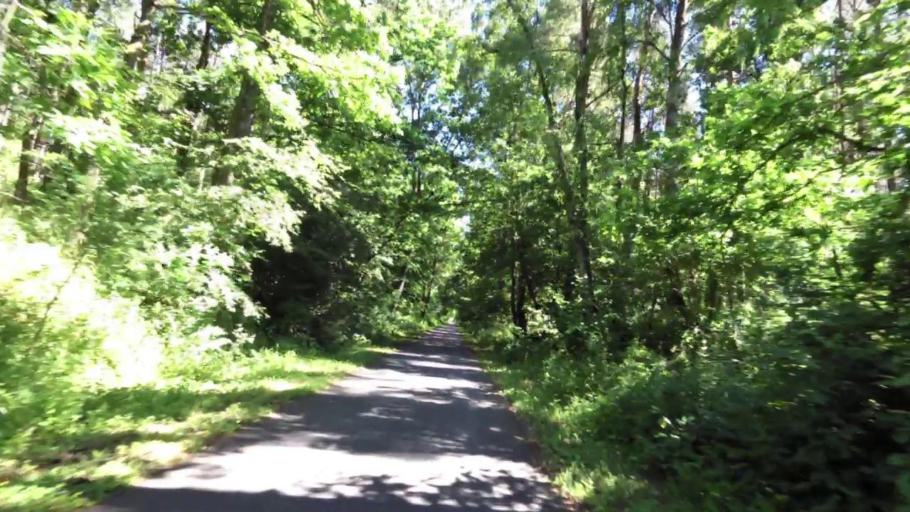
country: PL
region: West Pomeranian Voivodeship
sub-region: Powiat bialogardzki
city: Karlino
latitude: 54.0532
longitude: 15.8760
